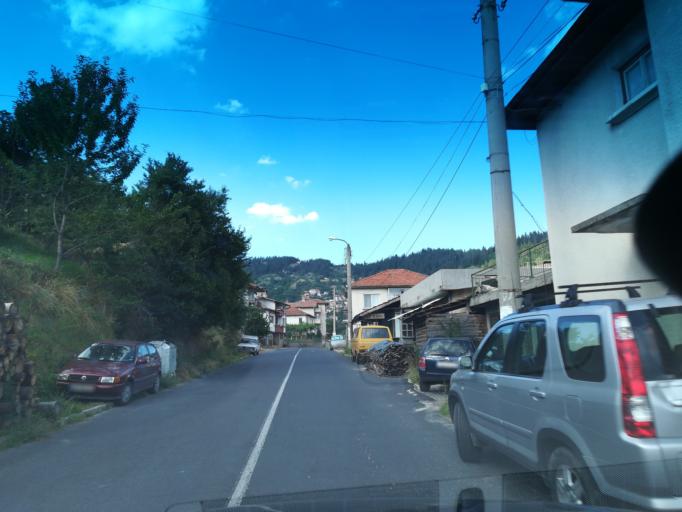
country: BG
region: Smolyan
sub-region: Obshtina Smolyan
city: Smolyan
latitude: 41.6551
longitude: 24.7734
